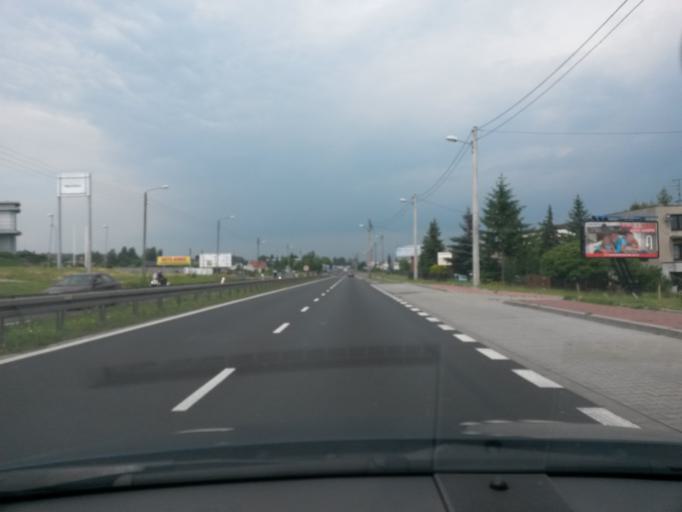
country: PL
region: Silesian Voivodeship
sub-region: Powiat czestochowski
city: Huta Stara B
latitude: 50.7595
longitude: 19.1595
